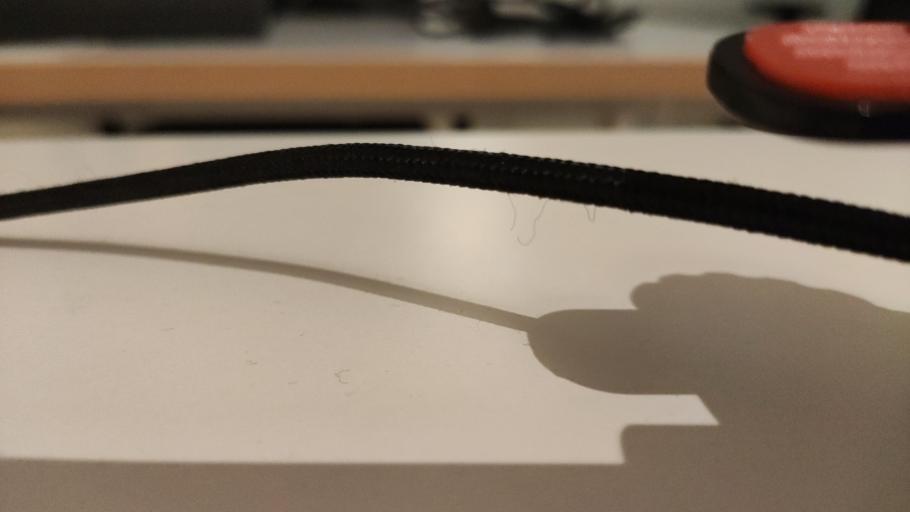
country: RU
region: Moskovskaya
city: Kurovskoye
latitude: 55.5501
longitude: 38.8736
